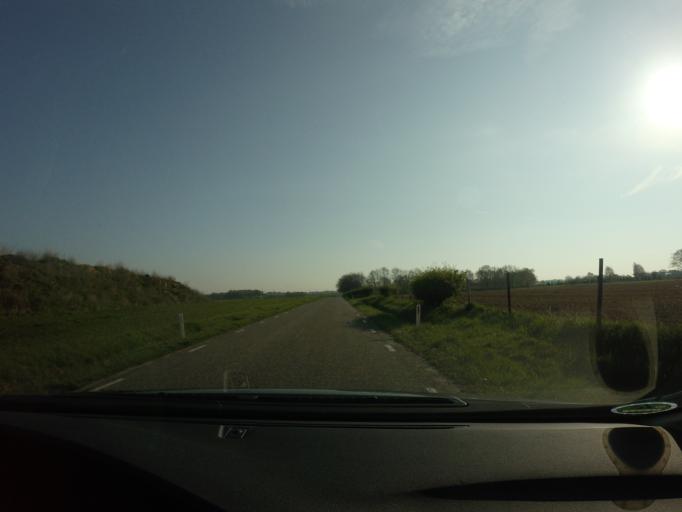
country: NL
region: Limburg
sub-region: Gemeente Beek
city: Beek
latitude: 50.9119
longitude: 5.7954
